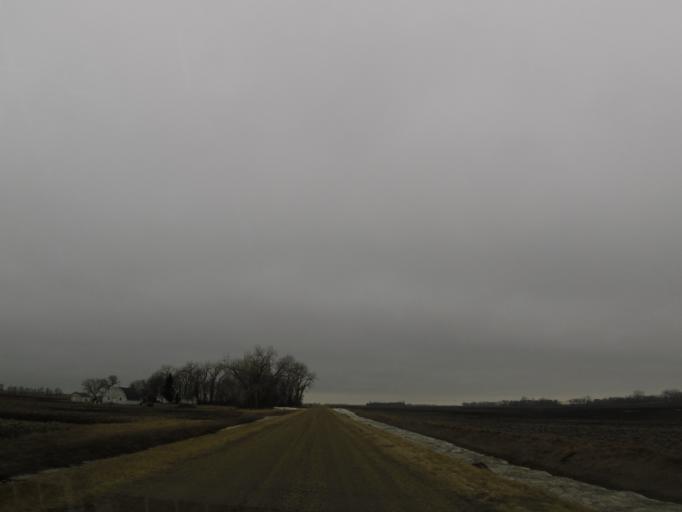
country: US
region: North Dakota
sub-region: Walsh County
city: Grafton
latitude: 48.3831
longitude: -97.1956
